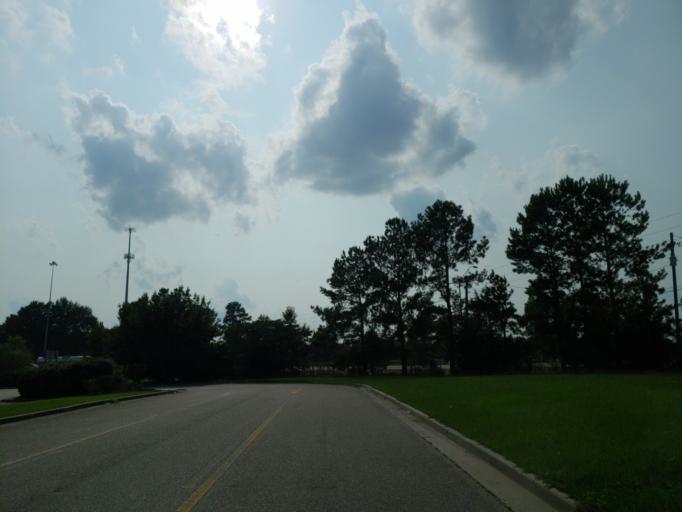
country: US
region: Mississippi
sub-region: Lamar County
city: West Hattiesburg
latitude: 31.3232
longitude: -89.3508
